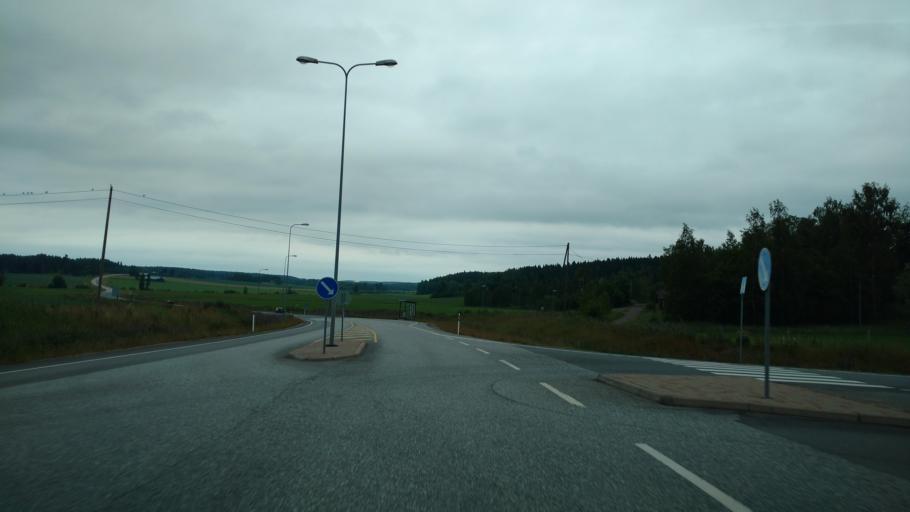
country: FI
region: Varsinais-Suomi
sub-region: Salo
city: Suomusjaervi
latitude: 60.3904
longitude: 23.5858
